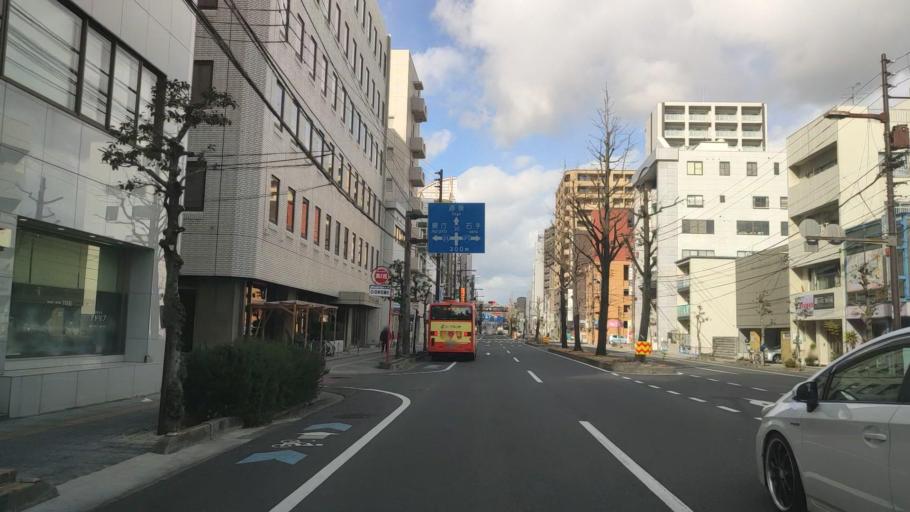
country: JP
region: Ehime
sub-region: Shikoku-chuo Shi
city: Matsuyama
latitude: 33.8389
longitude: 132.7753
